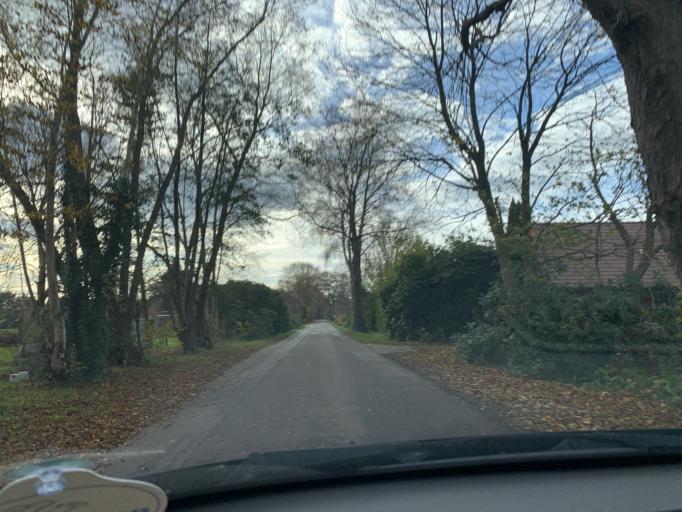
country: DE
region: Lower Saxony
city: Apen
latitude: 53.2245
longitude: 7.7874
